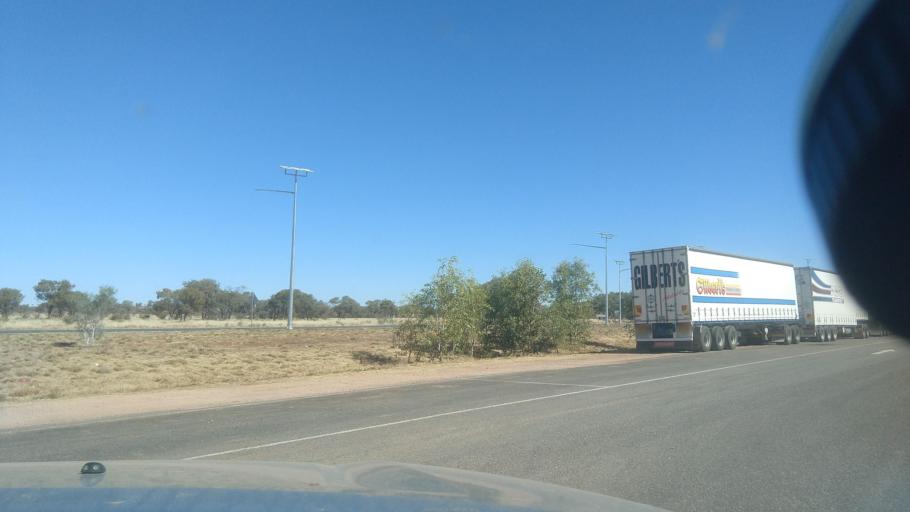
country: AU
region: Northern Territory
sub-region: Alice Springs
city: Alice Springs
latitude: -24.3405
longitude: 133.4583
